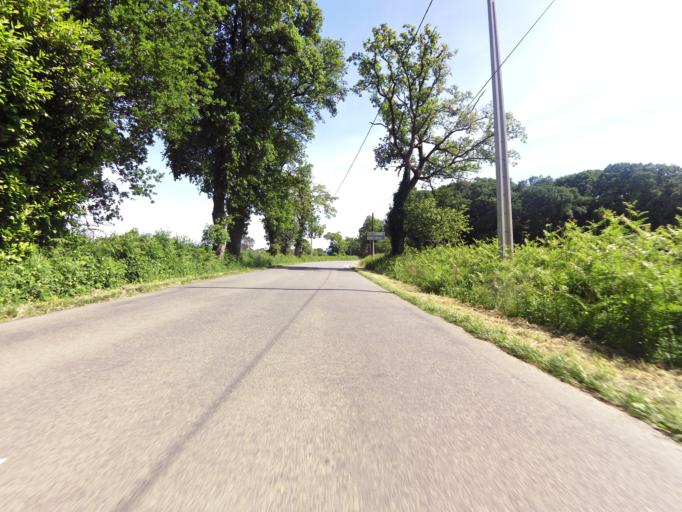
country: FR
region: Brittany
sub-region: Departement du Morbihan
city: Malansac
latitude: 47.6896
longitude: -2.3046
